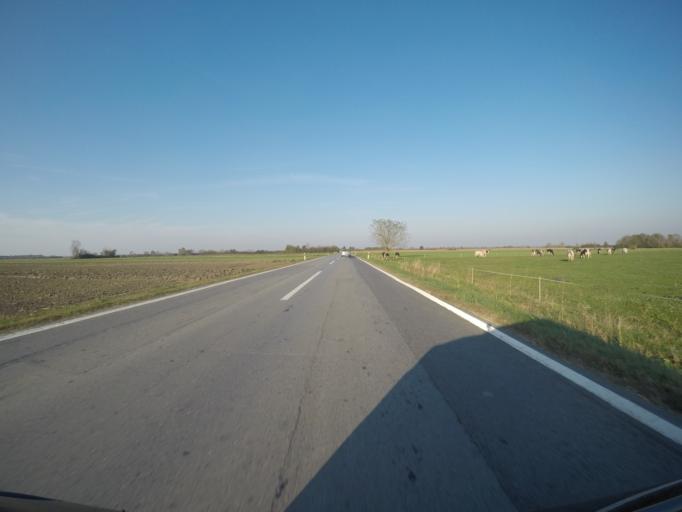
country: HU
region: Somogy
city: Barcs
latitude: 45.9162
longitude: 17.4483
